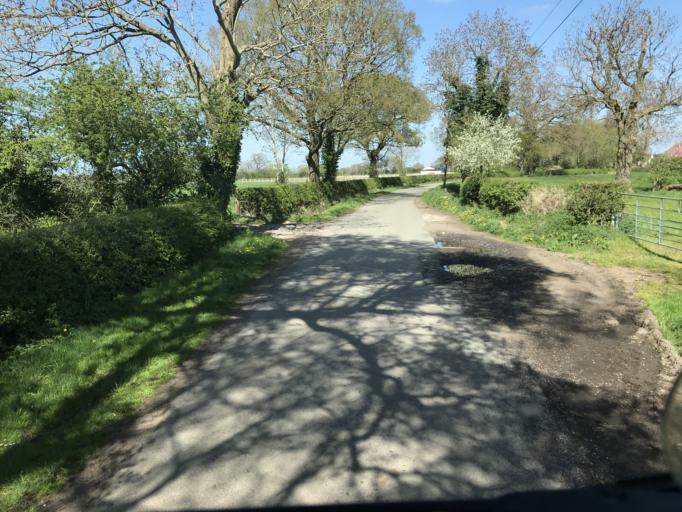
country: GB
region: England
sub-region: Cheshire East
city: Nantwich
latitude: 53.1074
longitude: -2.5312
